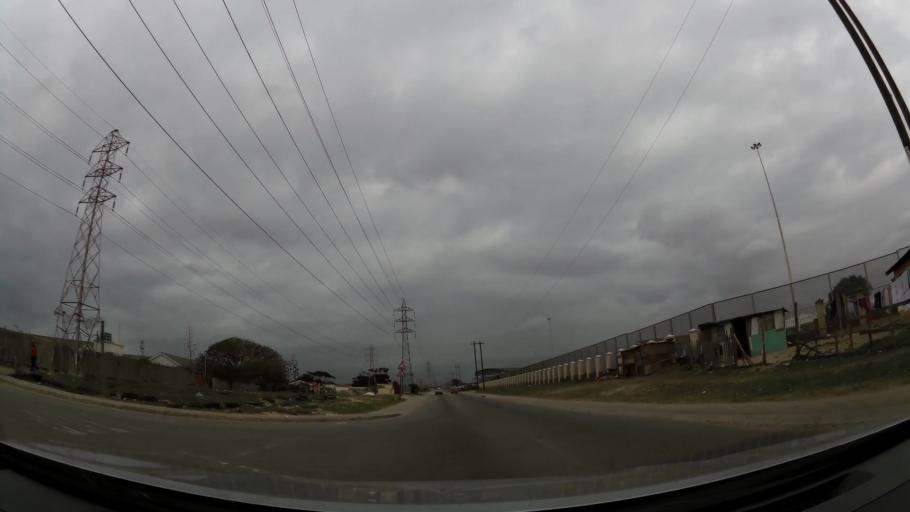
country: ZA
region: Eastern Cape
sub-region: Nelson Mandela Bay Metropolitan Municipality
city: Port Elizabeth
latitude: -33.8769
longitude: 25.5851
